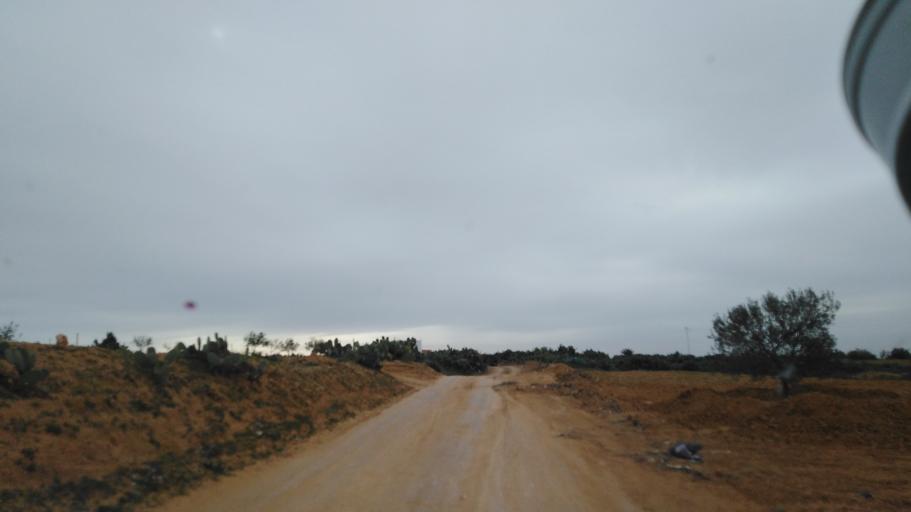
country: TN
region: Safaqis
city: Bi'r `Ali Bin Khalifah
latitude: 34.7667
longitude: 10.3764
